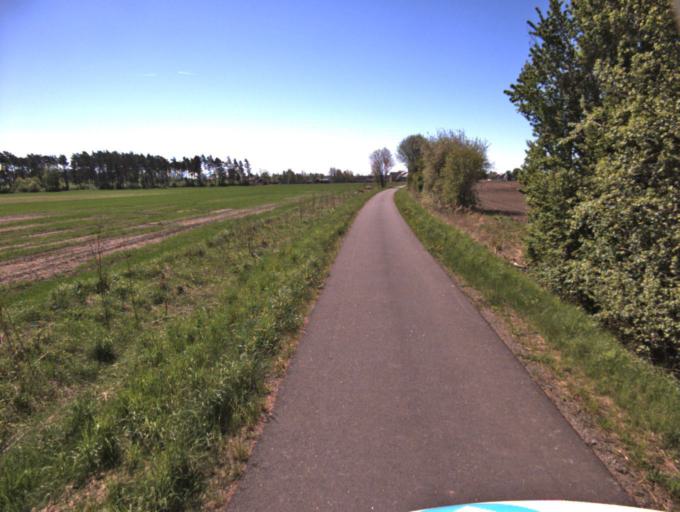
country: SE
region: Skane
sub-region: Kristianstads Kommun
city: Norra Asum
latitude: 55.9551
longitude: 14.1572
